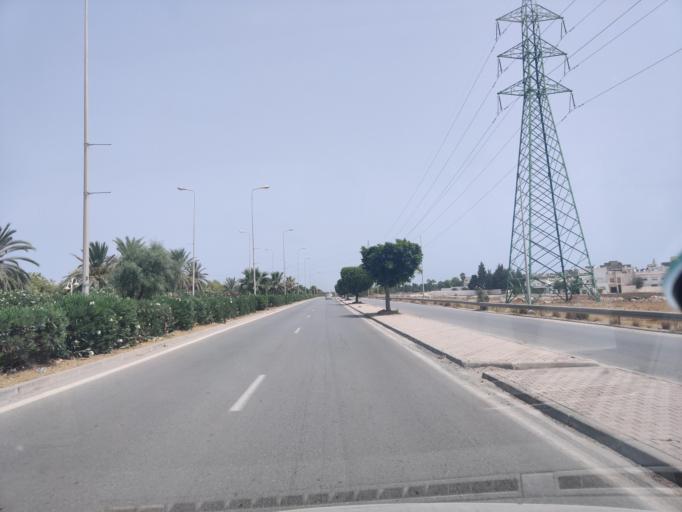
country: TN
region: Tunis
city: Carthage
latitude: 36.8524
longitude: 10.3072
